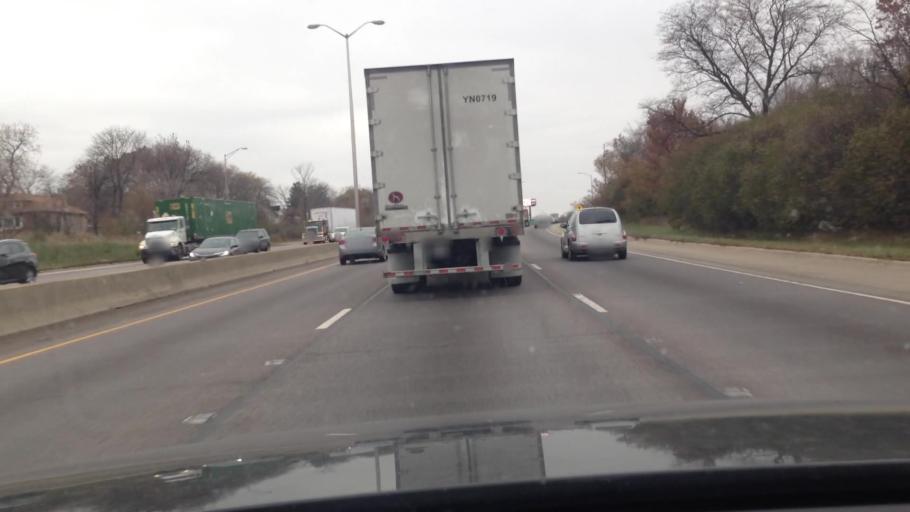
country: US
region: Illinois
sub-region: Cook County
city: Broadview
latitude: 41.8710
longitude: -87.8544
